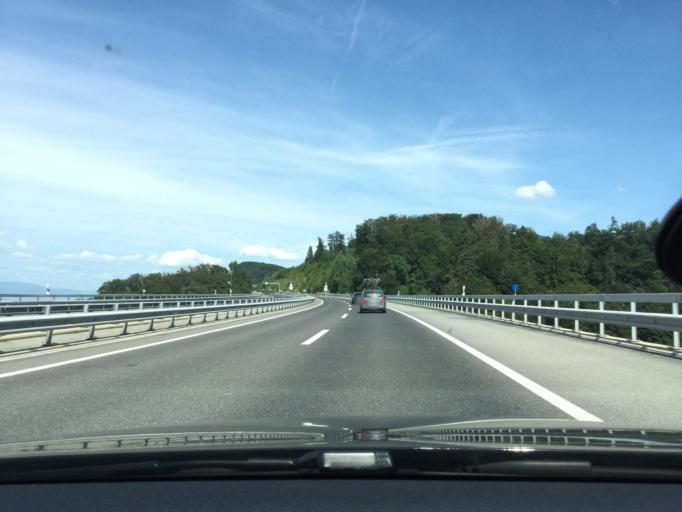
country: CH
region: Vaud
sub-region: Jura-Nord vaudois District
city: Yvonand
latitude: 46.7838
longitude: 6.7446
